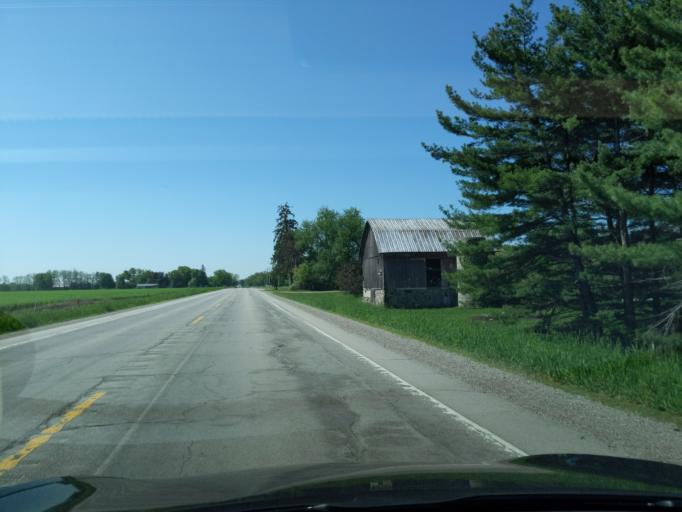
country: US
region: Michigan
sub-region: Ingham County
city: Stockbridge
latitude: 42.5063
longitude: -84.1902
